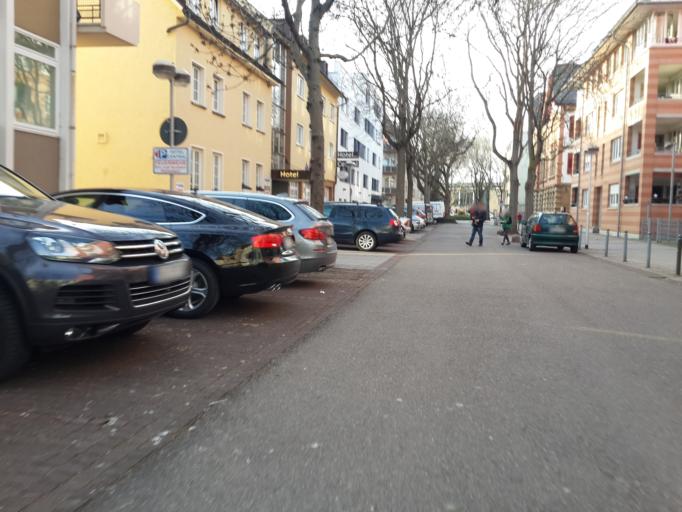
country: DE
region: Baden-Wuerttemberg
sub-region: Regierungsbezirk Stuttgart
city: Heilbronn
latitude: 49.1417
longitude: 9.2105
